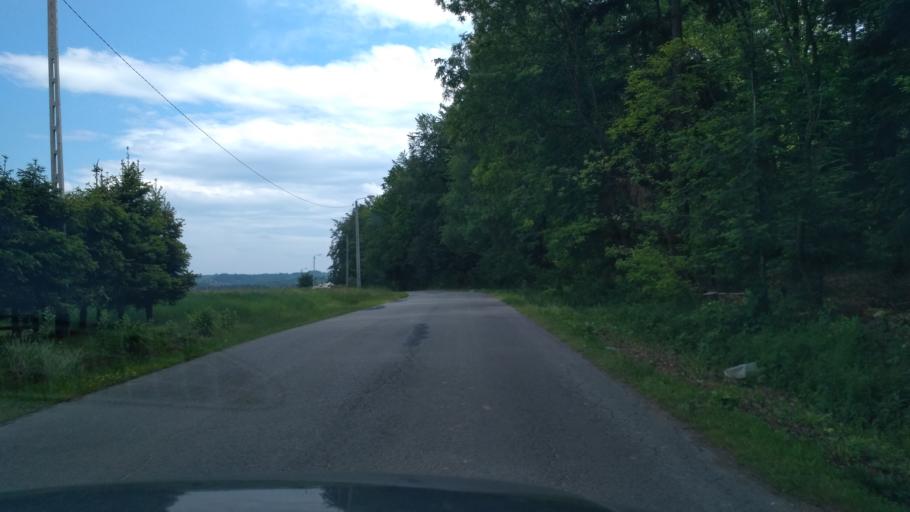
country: PL
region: Subcarpathian Voivodeship
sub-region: Powiat ropczycko-sedziszowski
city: Ropczyce
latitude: 50.0089
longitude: 21.6122
